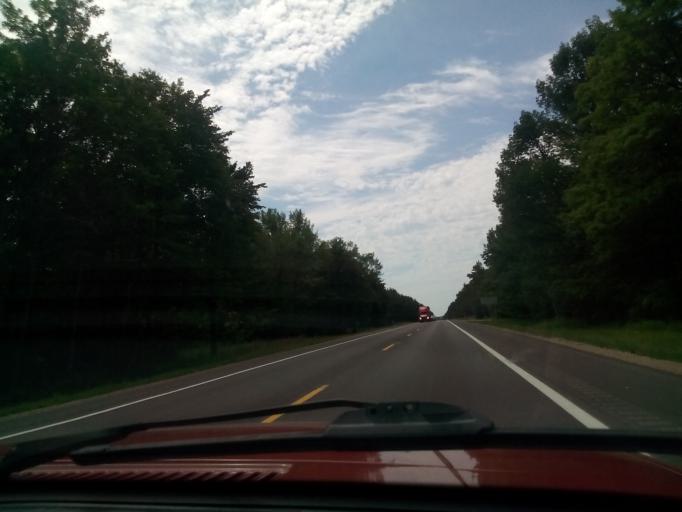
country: US
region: Michigan
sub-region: Schoolcraft County
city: Manistique
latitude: 46.0547
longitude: -85.9622
